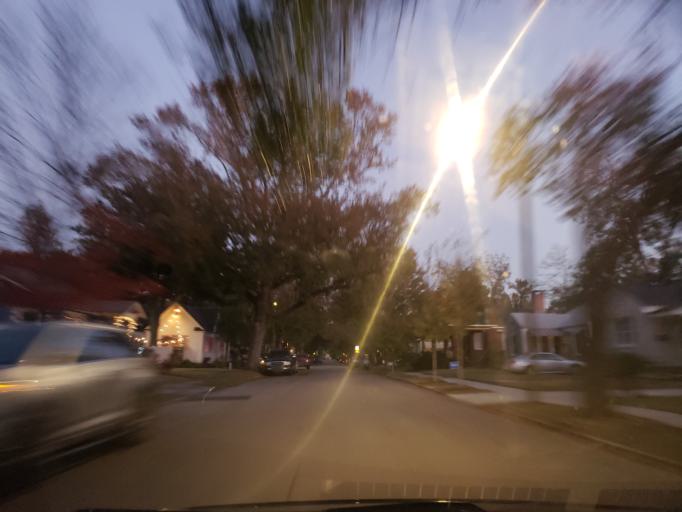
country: US
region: Georgia
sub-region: Chatham County
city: Thunderbolt
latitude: 32.0430
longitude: -81.0820
